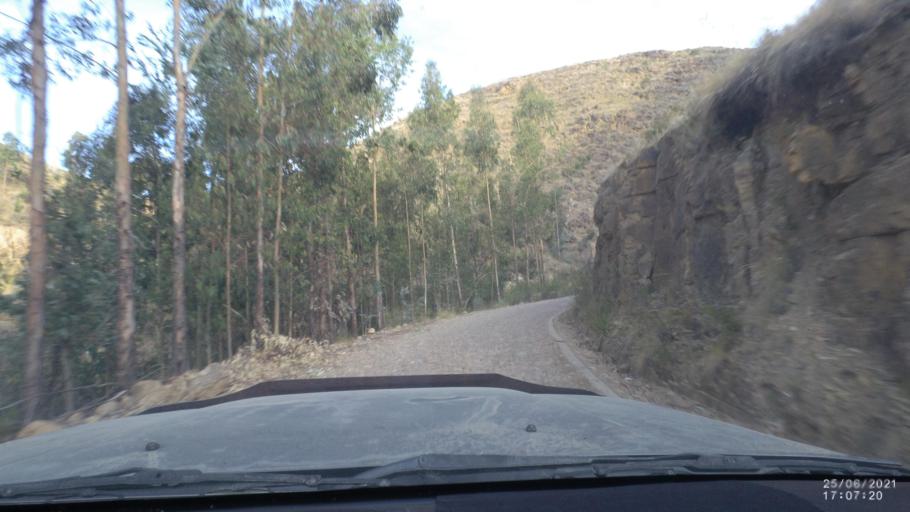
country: BO
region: Cochabamba
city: Arani
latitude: -17.8384
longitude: -65.7115
